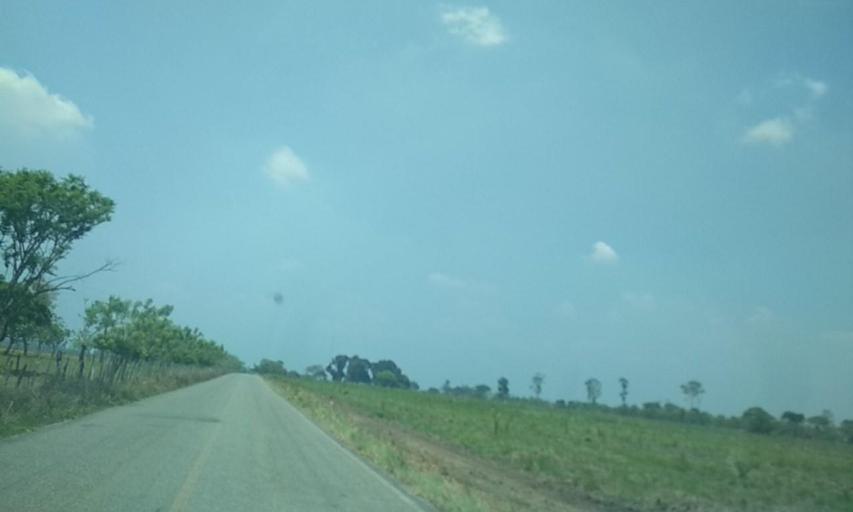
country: MX
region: Tabasco
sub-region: Huimanguillo
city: Paso de la Mina 3ra. Seccion
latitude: 17.8326
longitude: -93.6165
